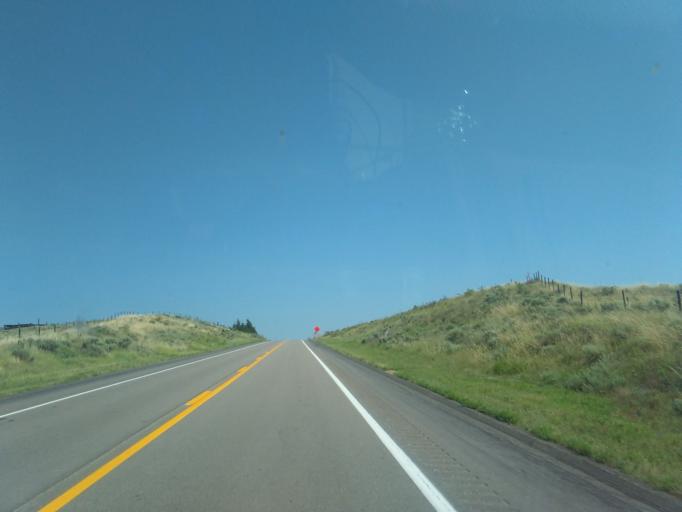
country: US
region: Nebraska
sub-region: Dundy County
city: Benkelman
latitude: 40.0148
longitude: -101.5426
